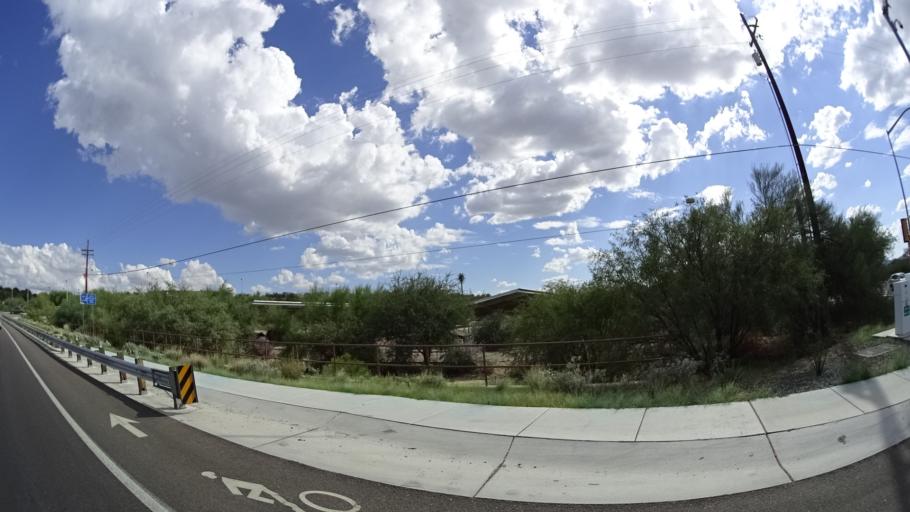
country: US
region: Arizona
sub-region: Pima County
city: Casas Adobes
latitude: 32.3479
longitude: -111.0246
